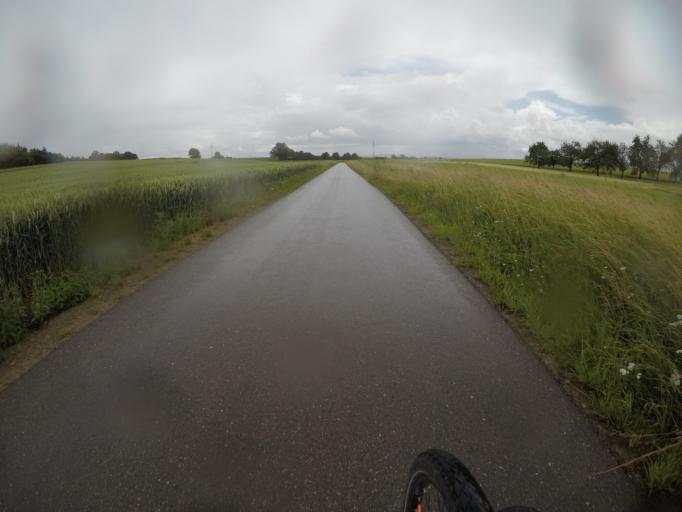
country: DE
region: Baden-Wuerttemberg
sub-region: Regierungsbezirk Stuttgart
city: Motzingen
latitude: 48.5110
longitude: 8.7949
